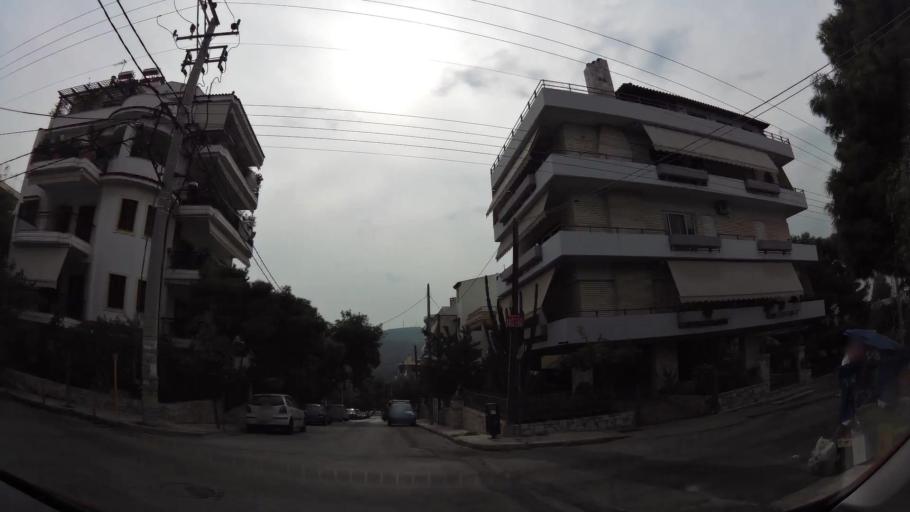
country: GR
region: Attica
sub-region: Nomarchia Athinas
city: Chaidari
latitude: 38.0169
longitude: 23.6446
